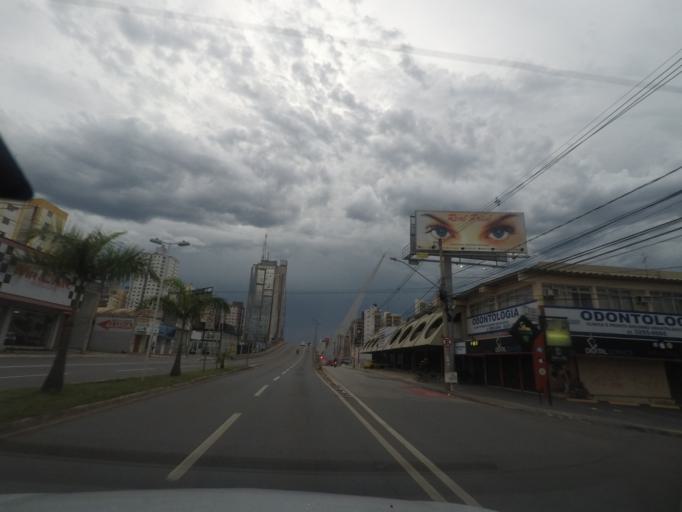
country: BR
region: Goias
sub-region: Goiania
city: Goiania
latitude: -16.7138
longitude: -49.2620
